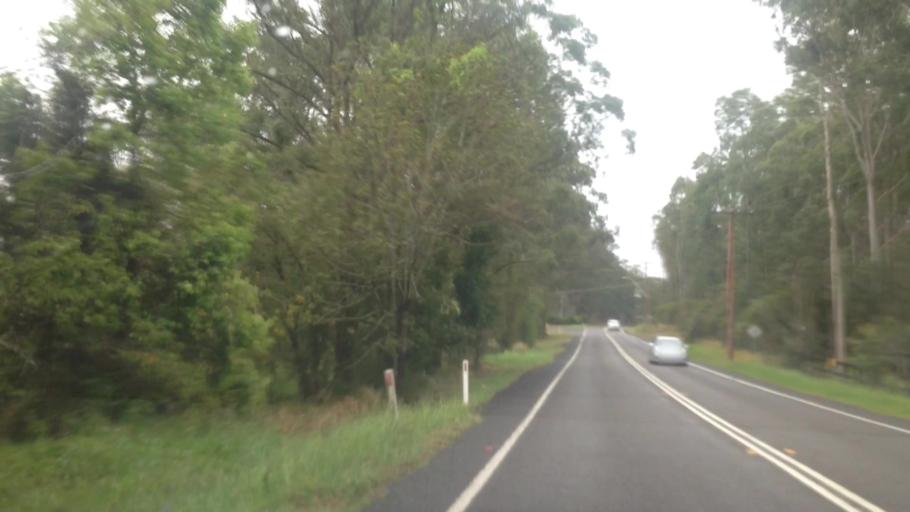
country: AU
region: New South Wales
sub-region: Wyong Shire
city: Little Jilliby
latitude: -33.2588
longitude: 151.3977
